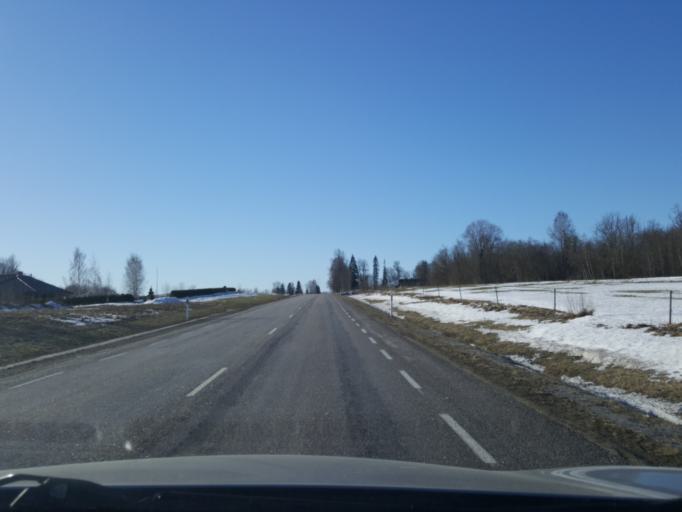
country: EE
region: Viljandimaa
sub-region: Viiratsi vald
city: Viiratsi
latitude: 58.4001
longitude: 25.6501
